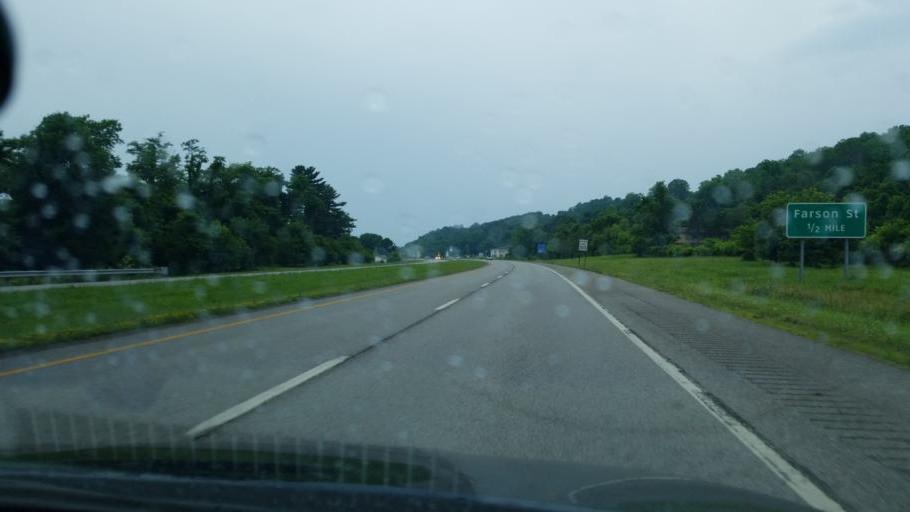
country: US
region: Ohio
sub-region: Washington County
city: Belpre
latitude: 39.2855
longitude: -81.6012
